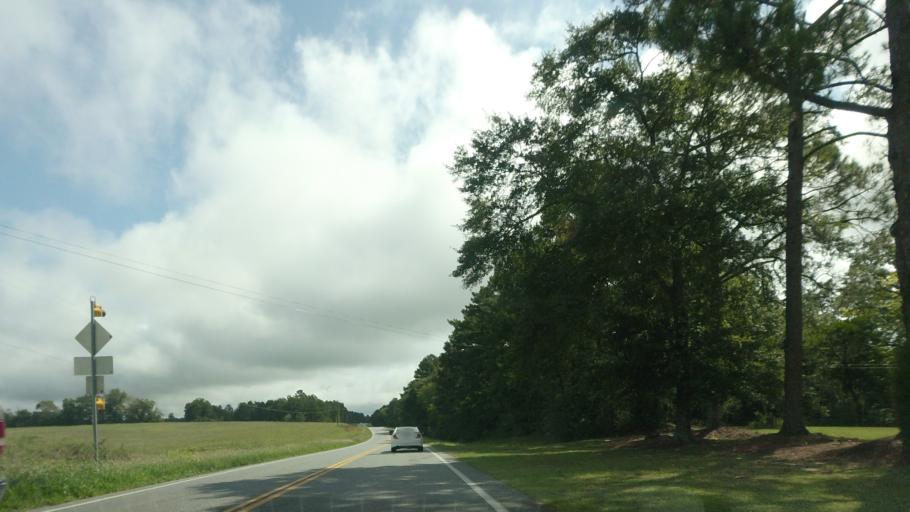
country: US
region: Georgia
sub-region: Laurens County
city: Dublin
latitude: 32.5465
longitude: -83.0174
